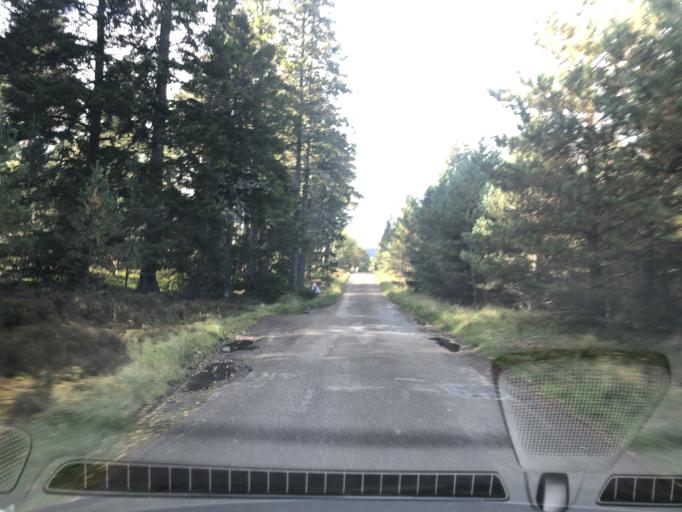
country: GB
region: Scotland
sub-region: Highland
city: Aviemore
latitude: 57.1137
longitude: -3.8931
